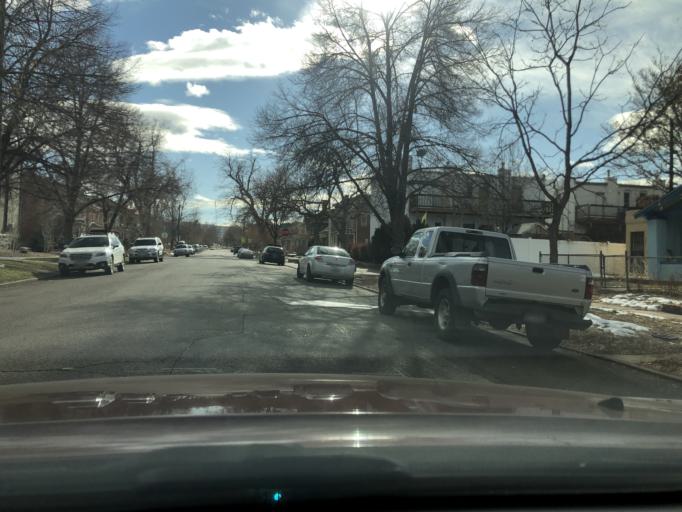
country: US
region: Colorado
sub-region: Denver County
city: Denver
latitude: 39.7551
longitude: -104.9721
